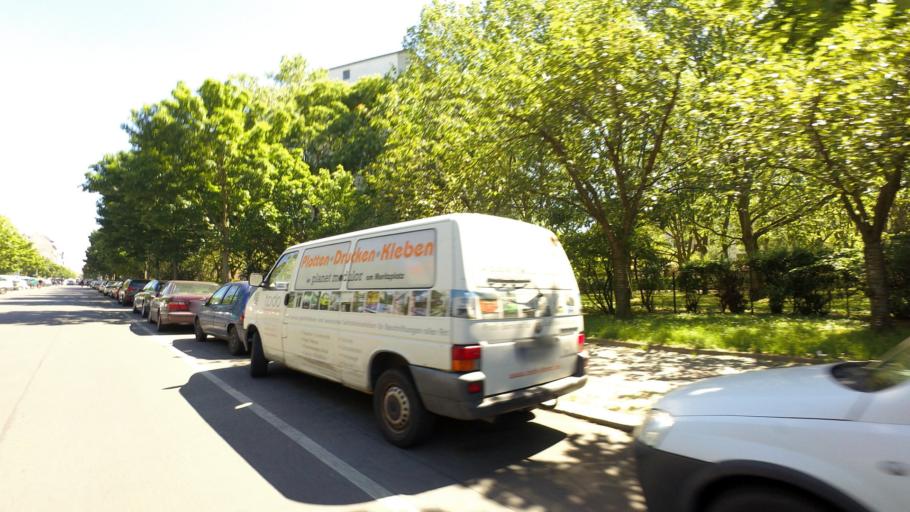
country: DE
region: Berlin
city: Bezirk Kreuzberg
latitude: 52.5023
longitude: 13.4071
